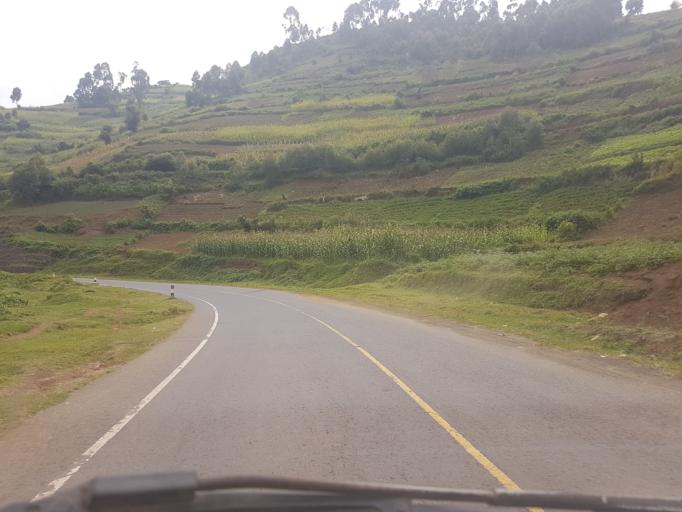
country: UG
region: Western Region
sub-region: Kisoro District
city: Kisoro
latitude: -1.2015
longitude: 29.8148
